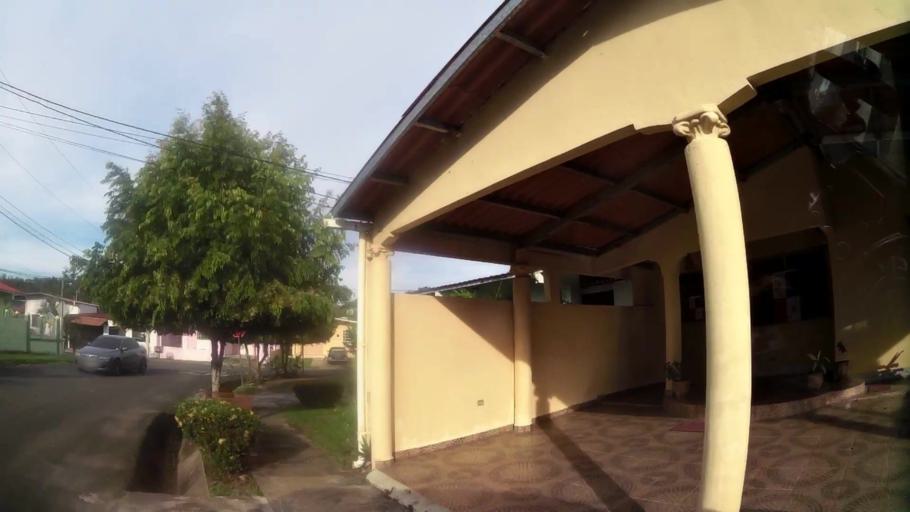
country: PA
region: Panama
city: La Chorrera
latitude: 8.8954
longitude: -79.7674
